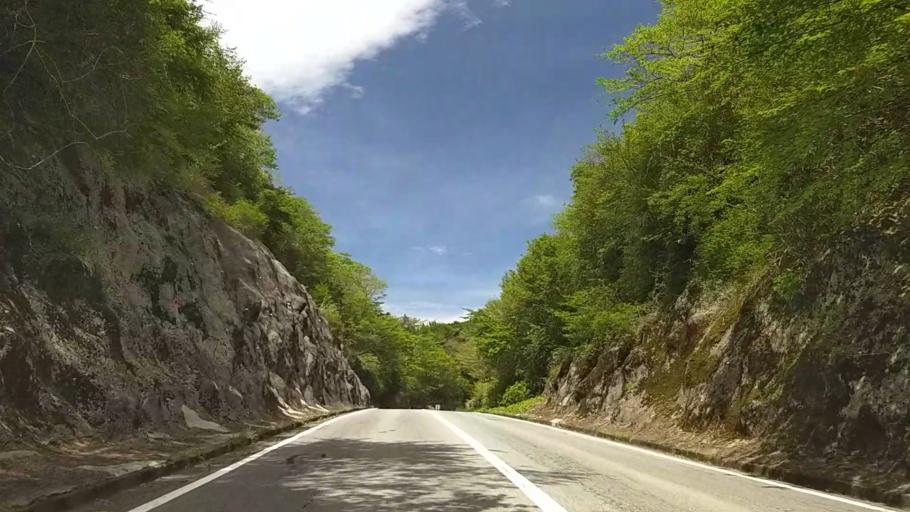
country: JP
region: Kanagawa
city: Hakone
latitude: 35.1939
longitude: 139.0654
